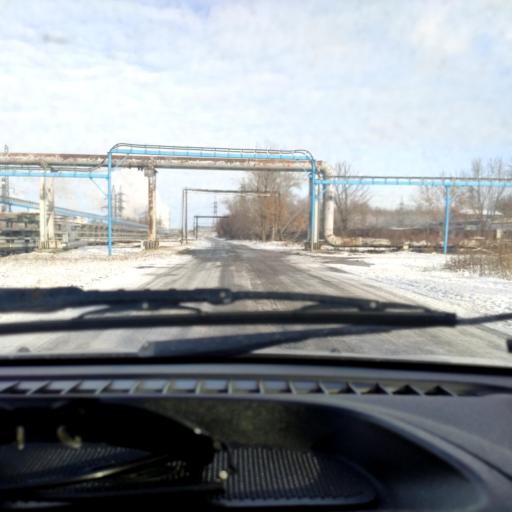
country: RU
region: Samara
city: Tol'yatti
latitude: 53.5375
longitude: 49.4835
